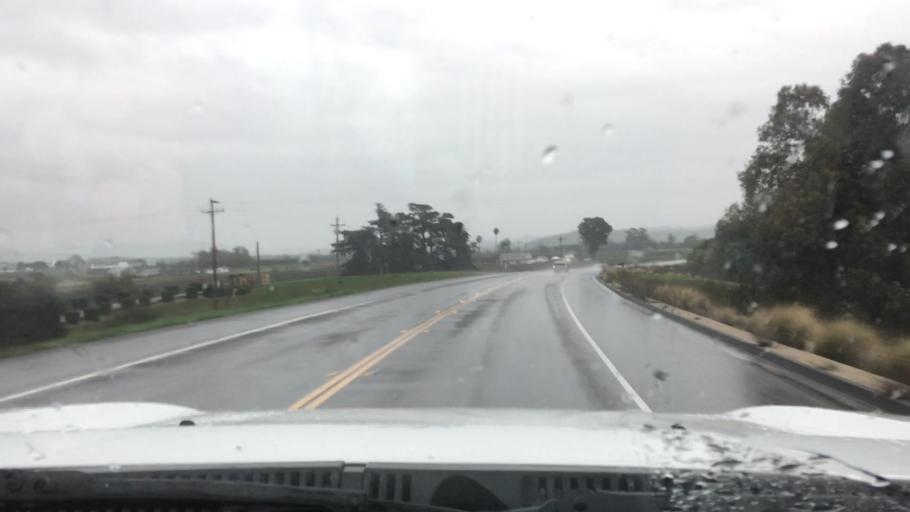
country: US
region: California
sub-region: San Luis Obispo County
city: San Luis Obispo
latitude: 35.2198
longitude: -120.6189
